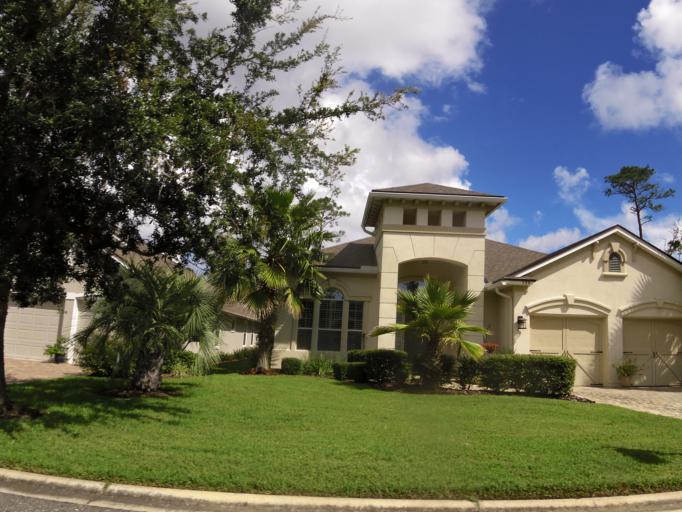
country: US
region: Florida
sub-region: Nassau County
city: Fernandina Beach
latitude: 30.6248
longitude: -81.4639
